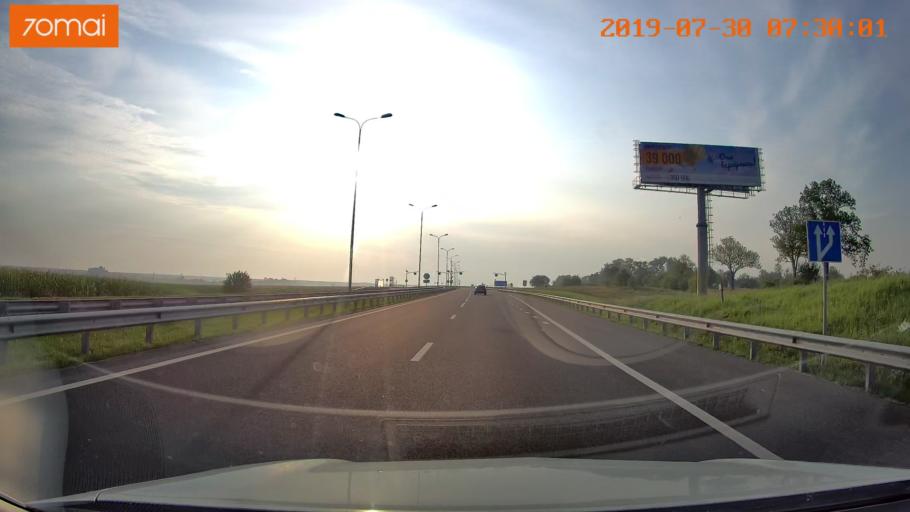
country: RU
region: Kaliningrad
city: Gvardeysk
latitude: 54.6704
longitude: 20.9549
